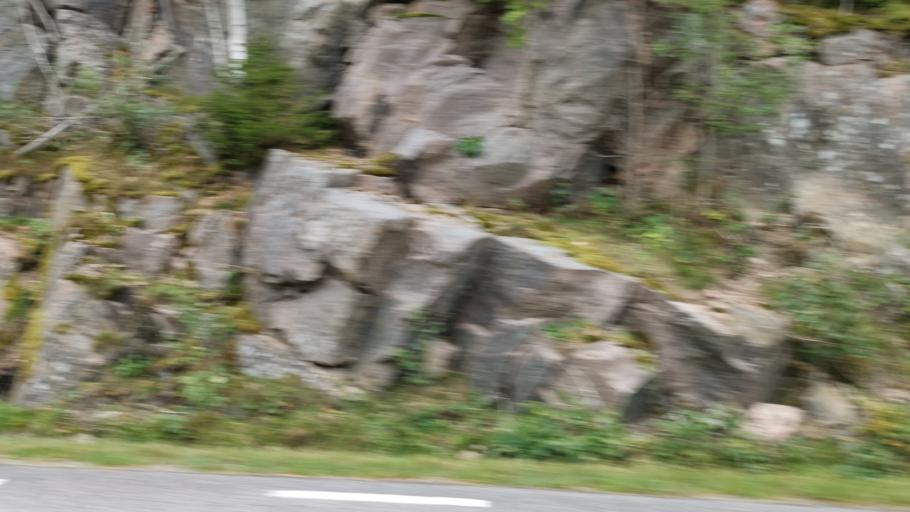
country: SE
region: Vaestra Goetaland
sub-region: Tanums Kommun
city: Tanumshede
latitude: 58.5822
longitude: 11.3554
